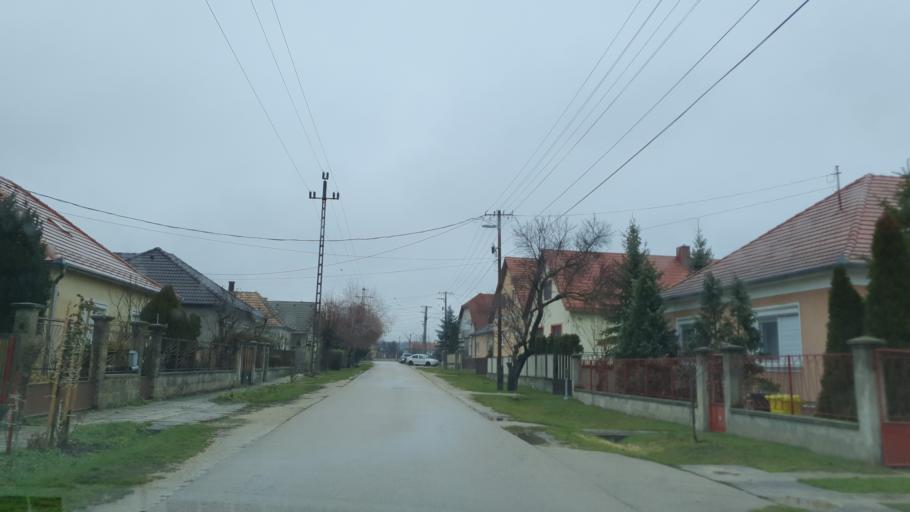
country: HU
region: Veszprem
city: Veszprem
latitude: 47.1426
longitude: 17.9425
